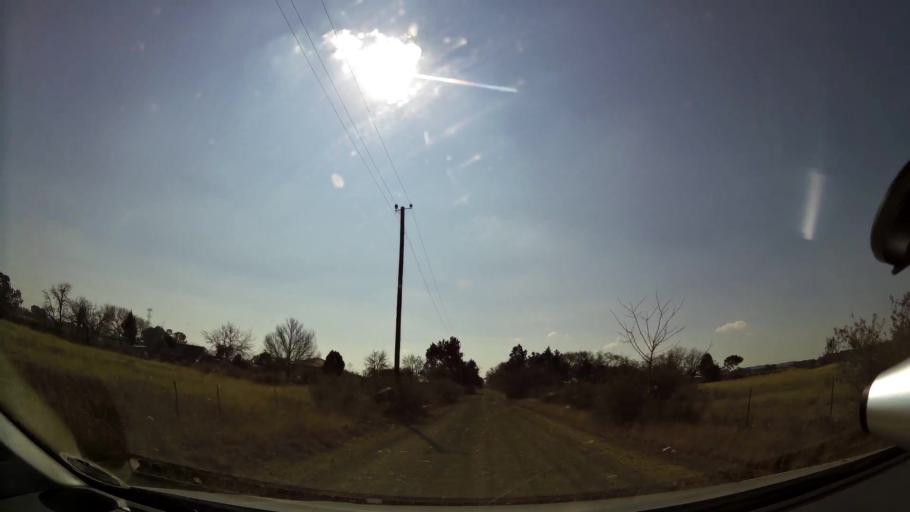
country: ZA
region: Orange Free State
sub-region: Mangaung Metropolitan Municipality
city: Bloemfontein
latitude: -29.1651
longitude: 26.3103
